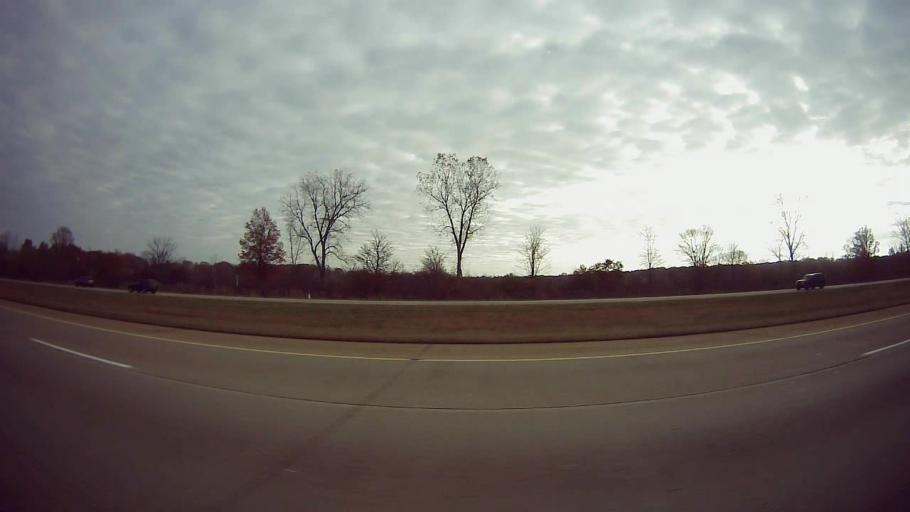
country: US
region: Michigan
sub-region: Monroe County
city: Carleton
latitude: 42.1073
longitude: -83.3780
